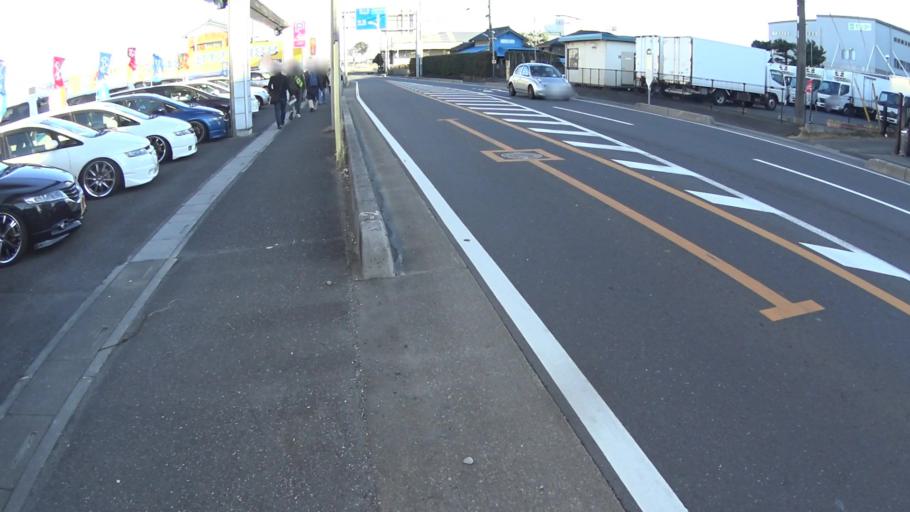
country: JP
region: Saitama
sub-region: Kawaguchi-shi
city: Hatogaya-honcho
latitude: 35.8893
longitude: 139.7214
